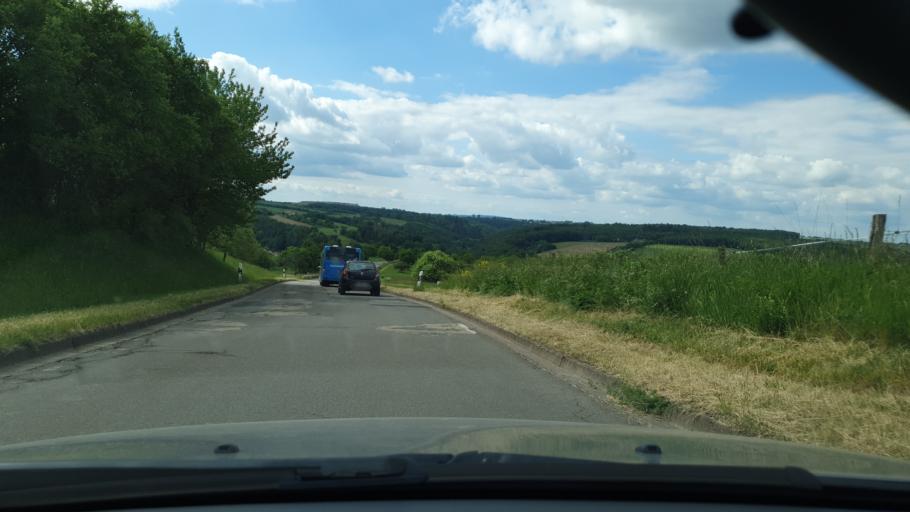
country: DE
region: Rheinland-Pfalz
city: Contwig
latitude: 49.2680
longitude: 7.4323
